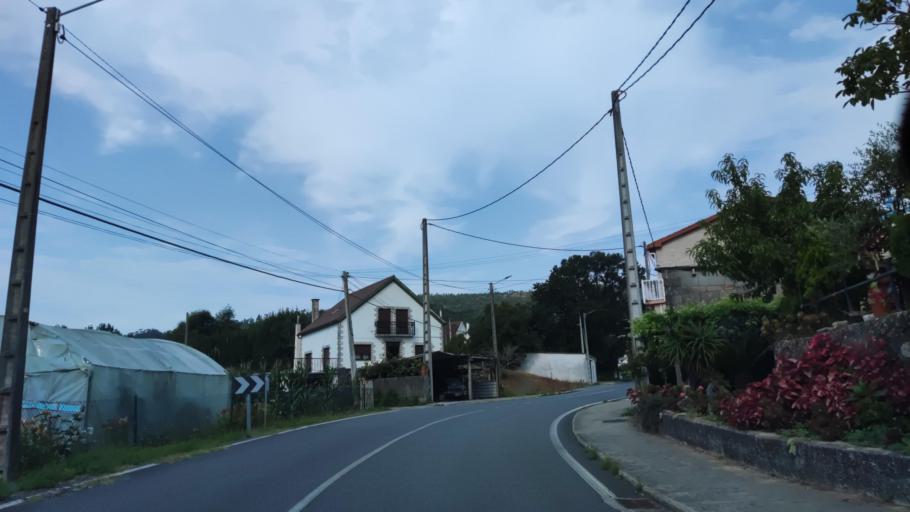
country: ES
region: Galicia
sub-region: Provincia da Coruna
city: Rianxo
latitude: 42.6539
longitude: -8.7711
